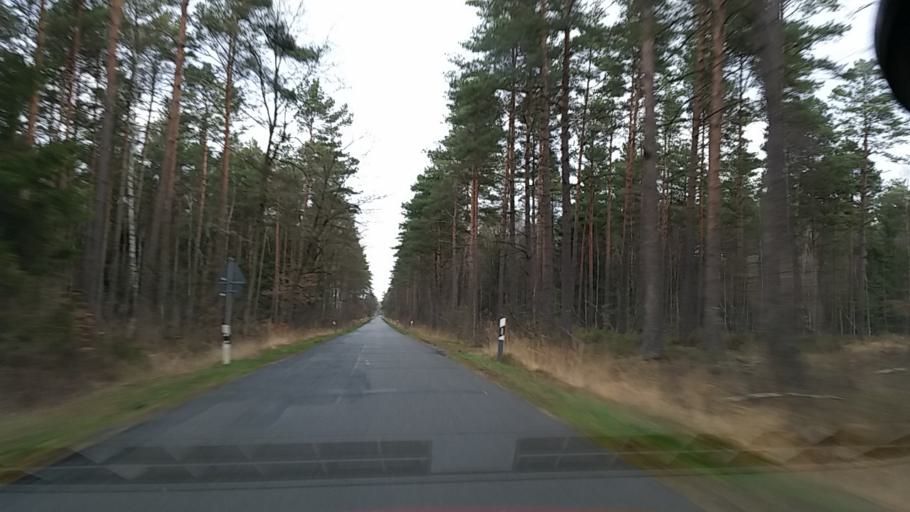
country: DE
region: Lower Saxony
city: Luder
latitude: 52.7794
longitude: 10.6677
